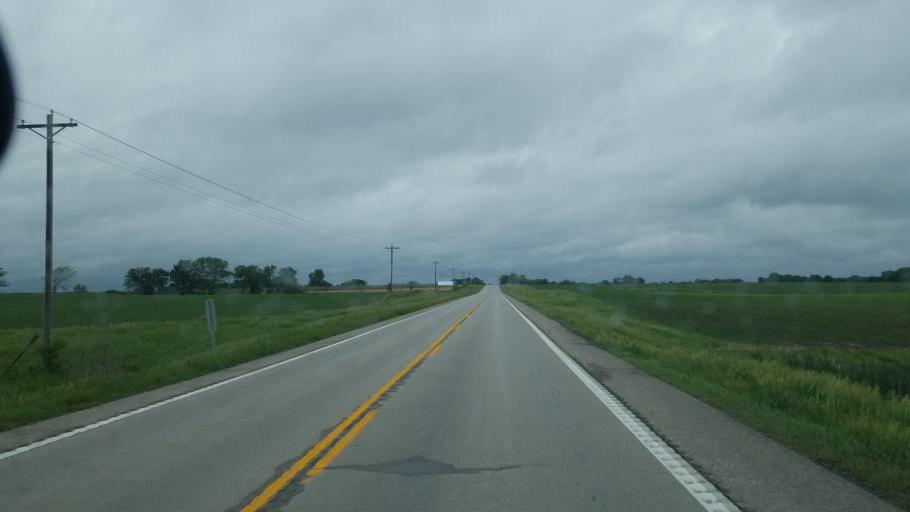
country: US
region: Missouri
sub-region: Livingston County
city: Chillicothe
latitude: 39.6488
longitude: -93.4789
